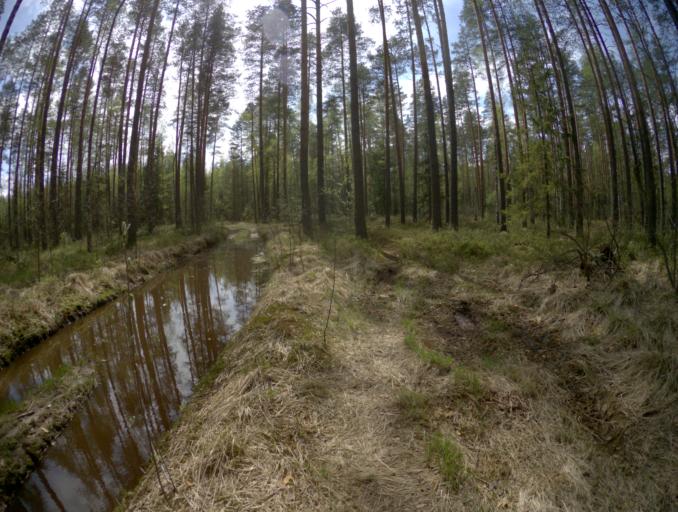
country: RU
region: Vladimir
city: Golovino
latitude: 55.9003
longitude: 40.3889
